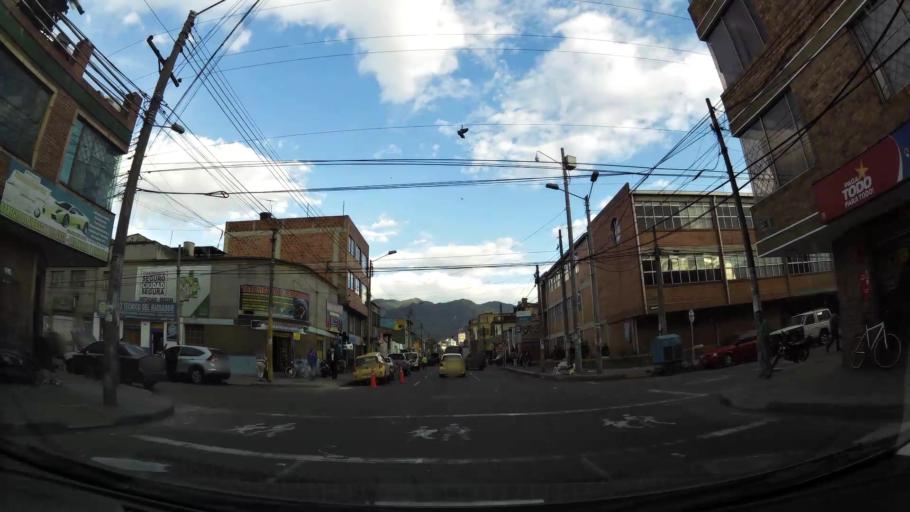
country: CO
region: Bogota D.C.
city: Bogota
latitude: 4.6606
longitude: -74.0752
